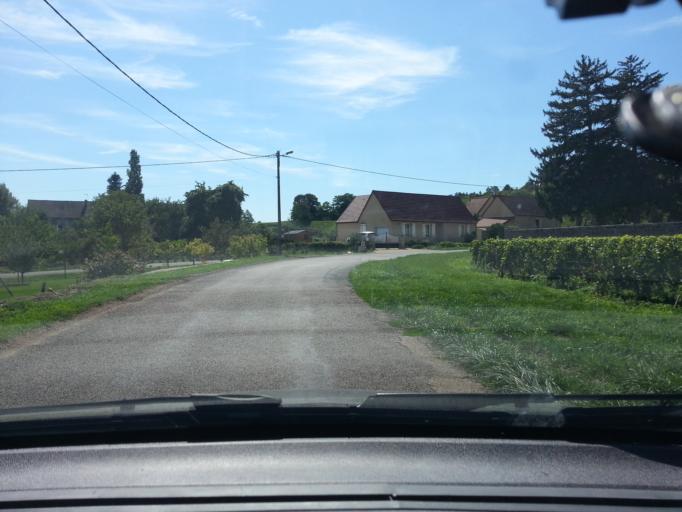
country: FR
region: Bourgogne
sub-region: Departement de Saone-et-Loire
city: Givry
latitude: 46.7760
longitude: 4.7238
